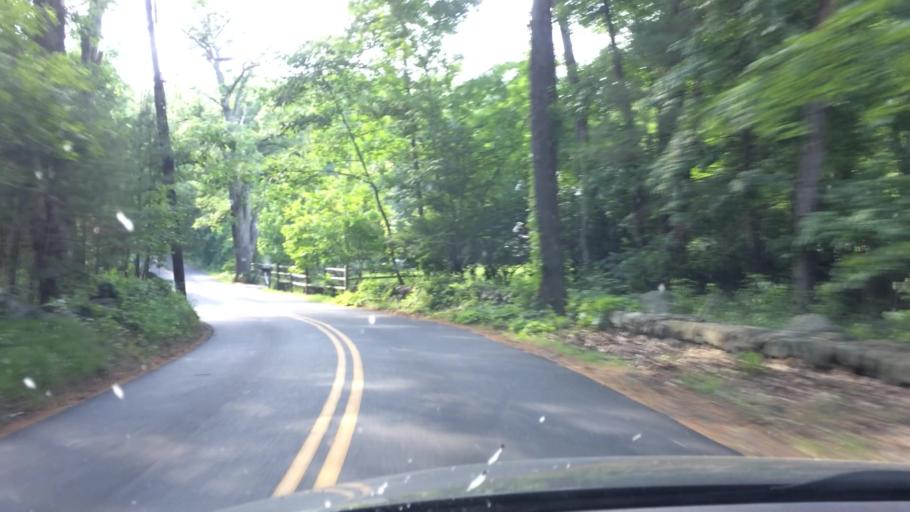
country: US
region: Massachusetts
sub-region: Middlesex County
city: Weston
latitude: 42.3839
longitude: -71.3252
